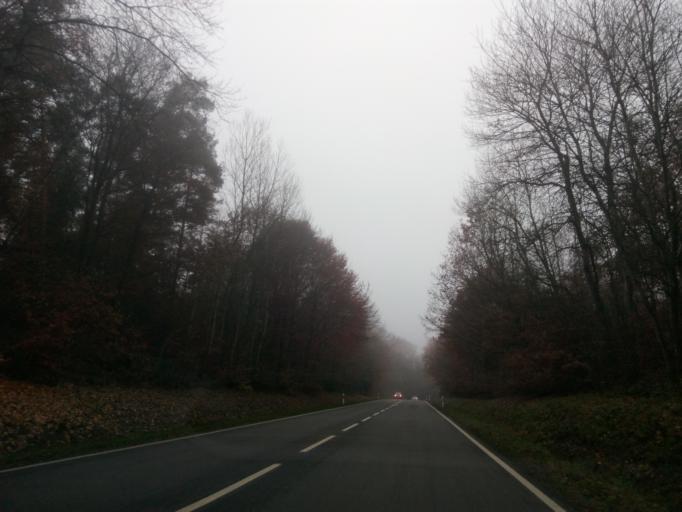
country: DE
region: Rheinland-Pfalz
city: Sienhachenbach
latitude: 49.7035
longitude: 7.4759
